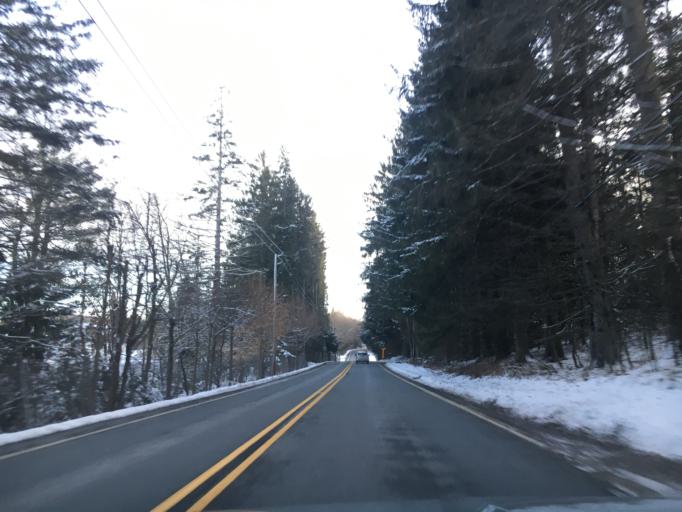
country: US
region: Pennsylvania
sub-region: Pike County
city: Hemlock Farms
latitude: 41.2483
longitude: -75.0690
